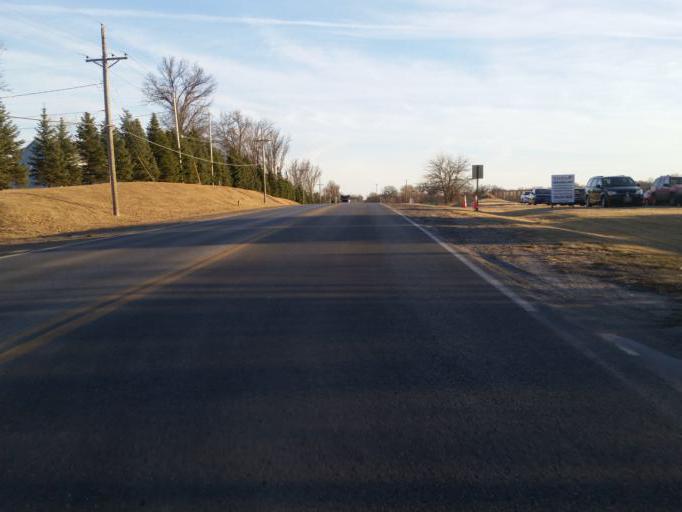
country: US
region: Nebraska
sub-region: Sarpy County
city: Offutt Air Force Base
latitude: 41.1258
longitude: -95.9666
